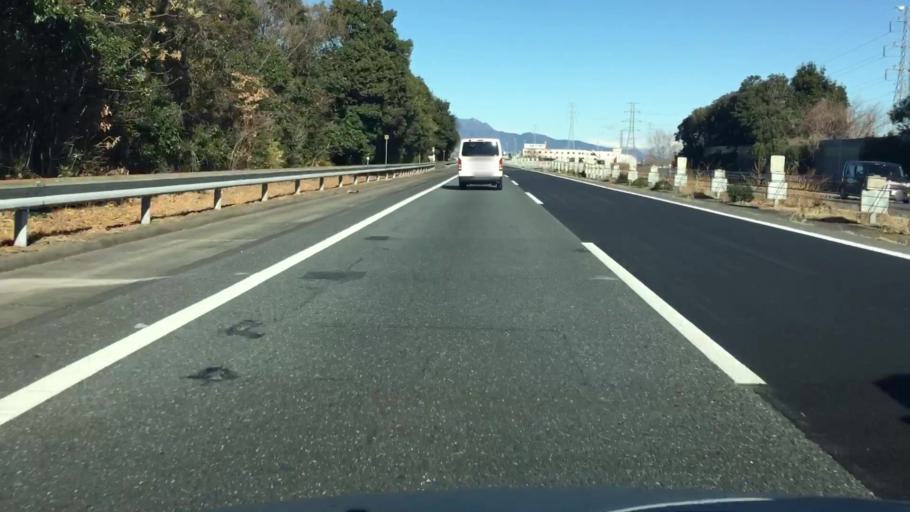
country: JP
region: Gunma
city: Kanekomachi
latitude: 36.3984
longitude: 139.0248
